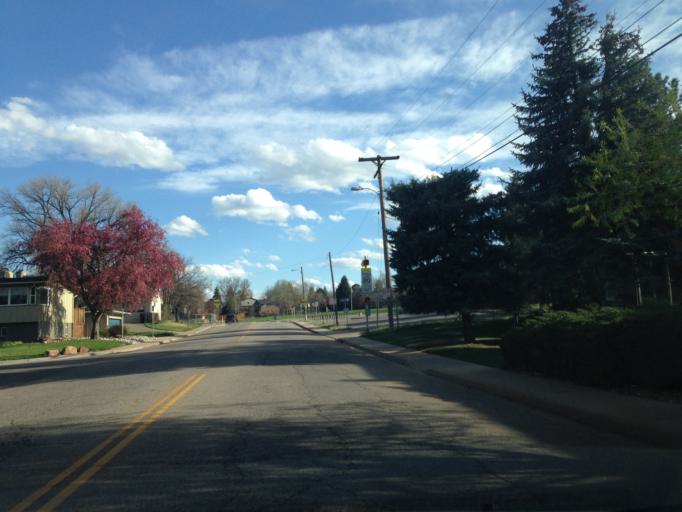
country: US
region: Colorado
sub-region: Boulder County
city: Boulder
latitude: 39.9822
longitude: -105.2513
